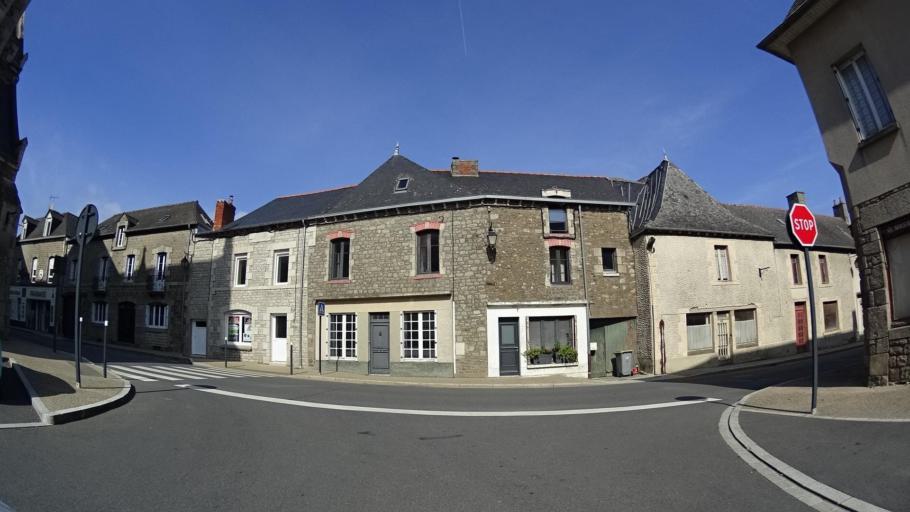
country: FR
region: Brittany
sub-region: Departement d'Ille-et-Vilaine
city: Medreac
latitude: 48.2674
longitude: -2.0652
